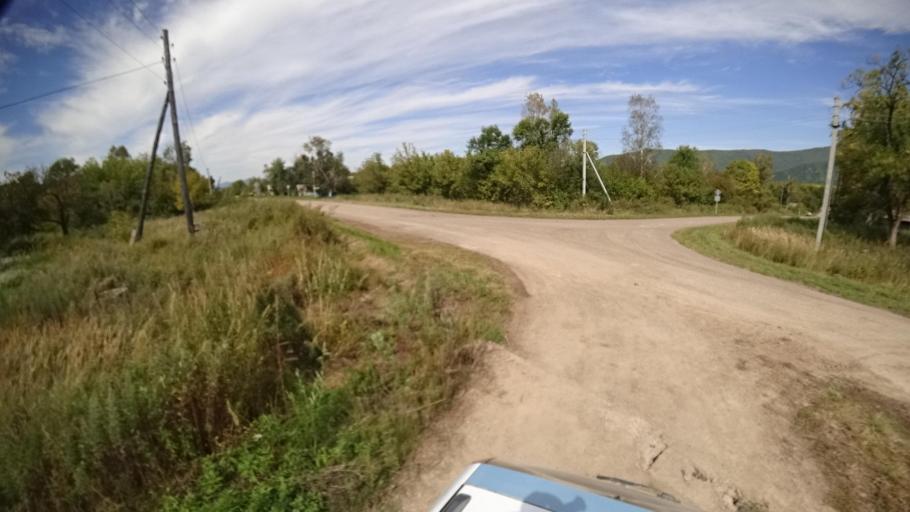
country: RU
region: Primorskiy
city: Yakovlevka
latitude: 44.6553
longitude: 133.7440
